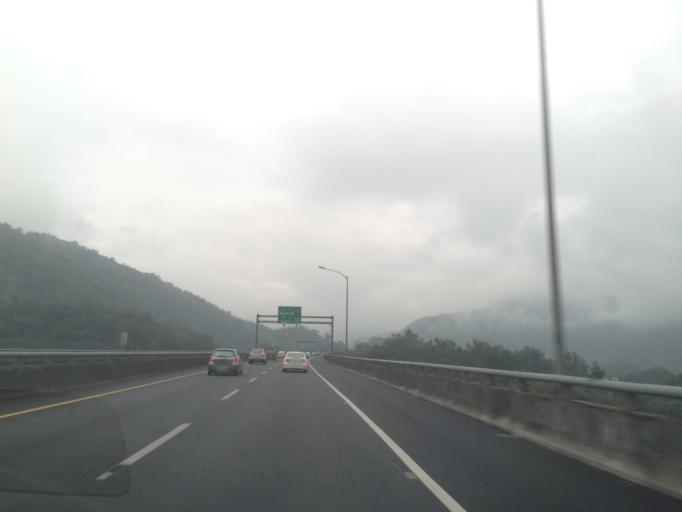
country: TW
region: Taiwan
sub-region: Nantou
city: Puli
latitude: 23.9792
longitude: 120.9013
